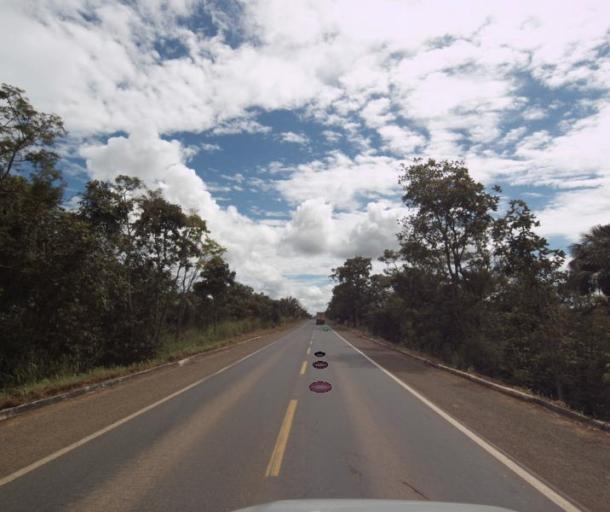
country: BR
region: Goias
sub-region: Uruacu
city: Uruacu
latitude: -14.4528
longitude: -49.1564
